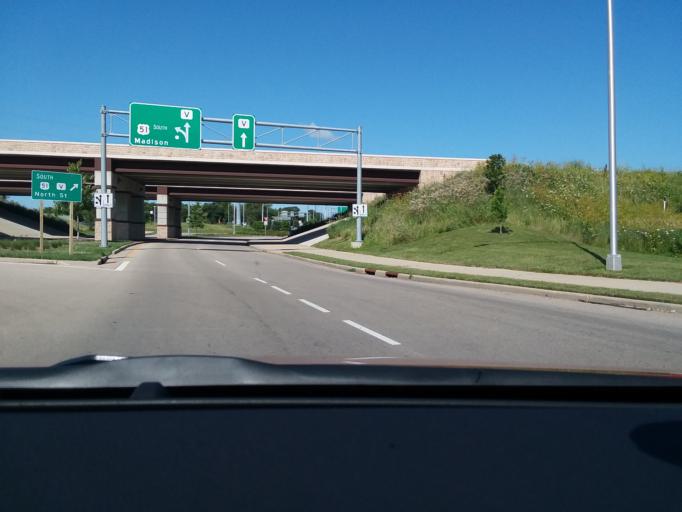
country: US
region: Wisconsin
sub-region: Dane County
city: De Forest
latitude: 43.2530
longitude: -89.3233
